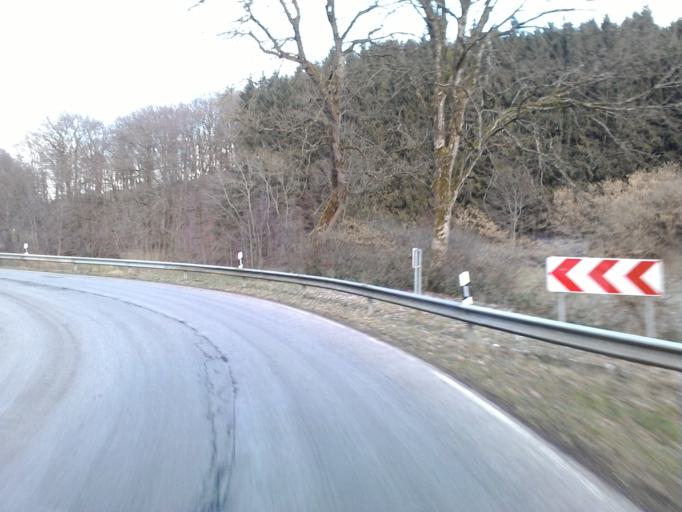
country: DE
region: Rheinland-Pfalz
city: Uppershausen
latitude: 50.0510
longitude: 6.3068
